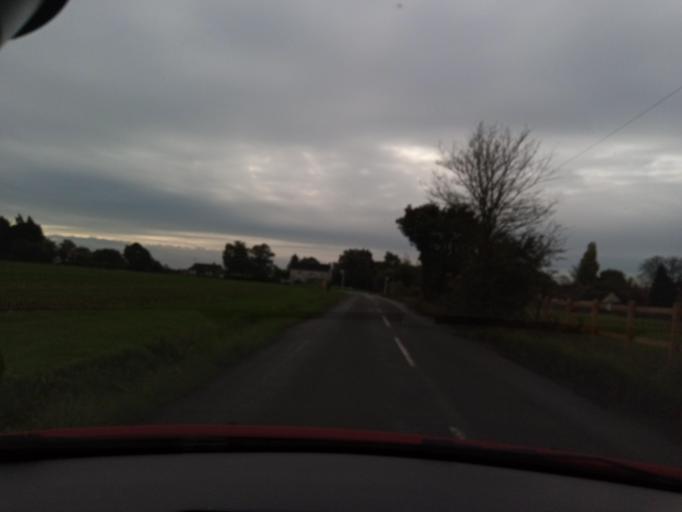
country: GB
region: England
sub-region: Essex
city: West Mersea
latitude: 51.7859
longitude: 0.9395
